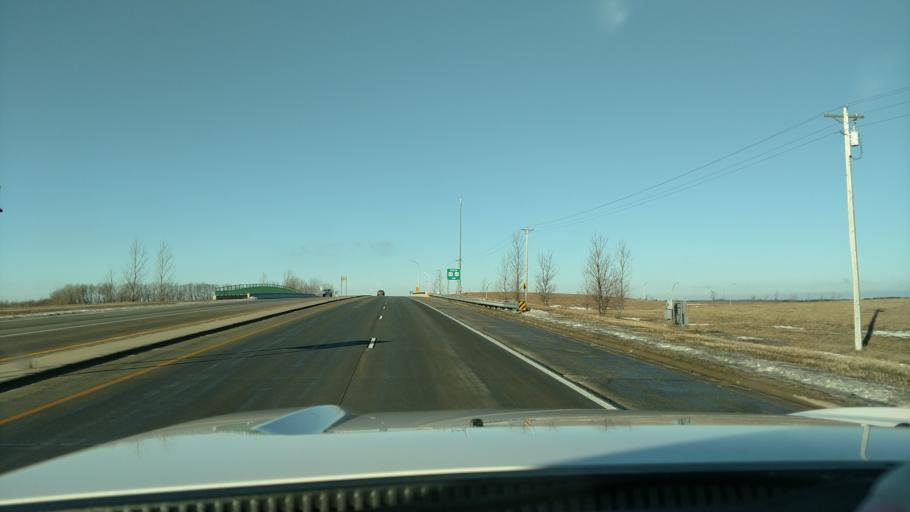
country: US
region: Minnesota
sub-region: Olmsted County
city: Oronoco
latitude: 44.1082
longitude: -92.5131
